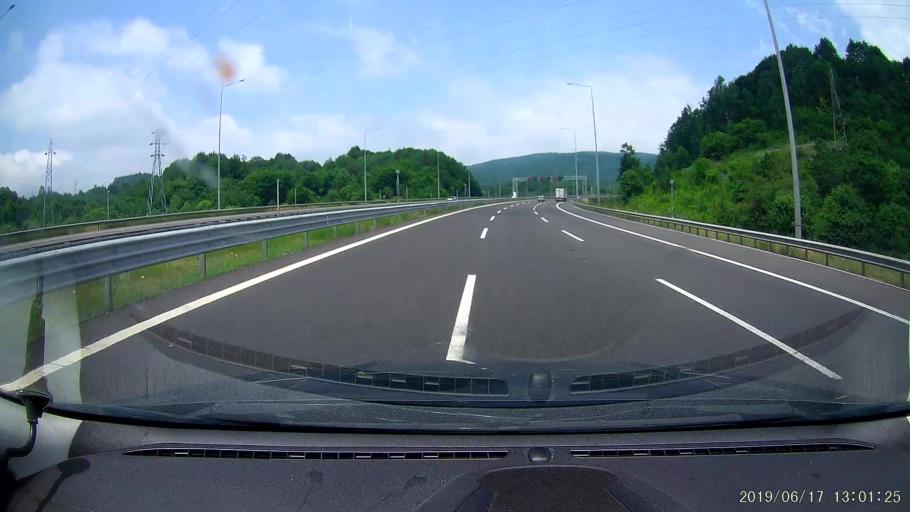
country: TR
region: Duzce
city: Kaynasli
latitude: 40.7268
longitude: 31.4458
